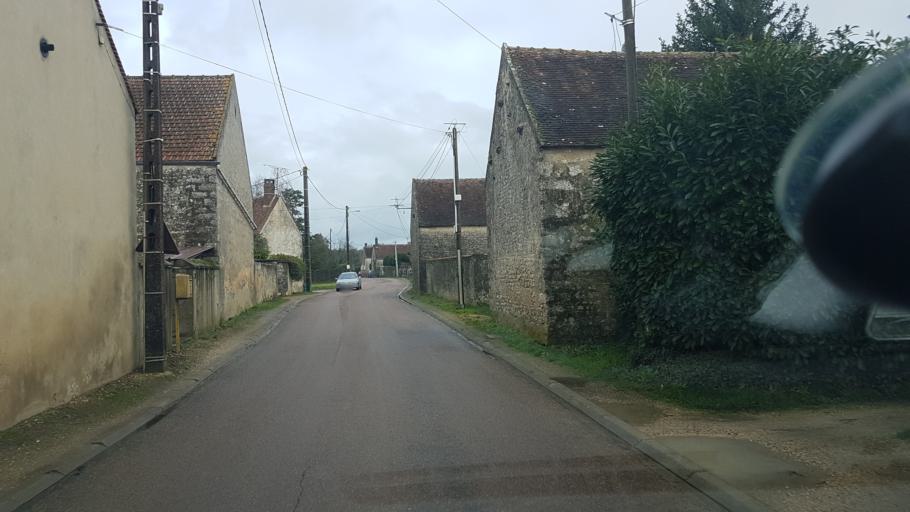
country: FR
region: Ile-de-France
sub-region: Departement de Seine-et-Marne
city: Souppes-sur-Loing
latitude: 48.2235
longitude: 2.7968
